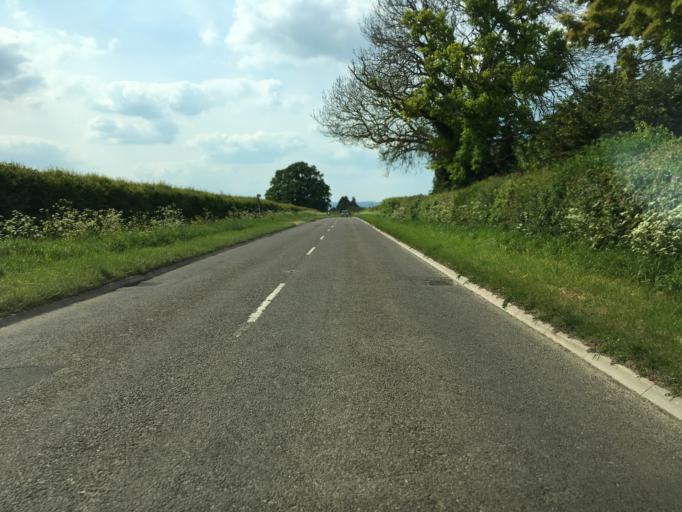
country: GB
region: England
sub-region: South Gloucestershire
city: Thornbury
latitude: 51.6258
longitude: -2.5321
